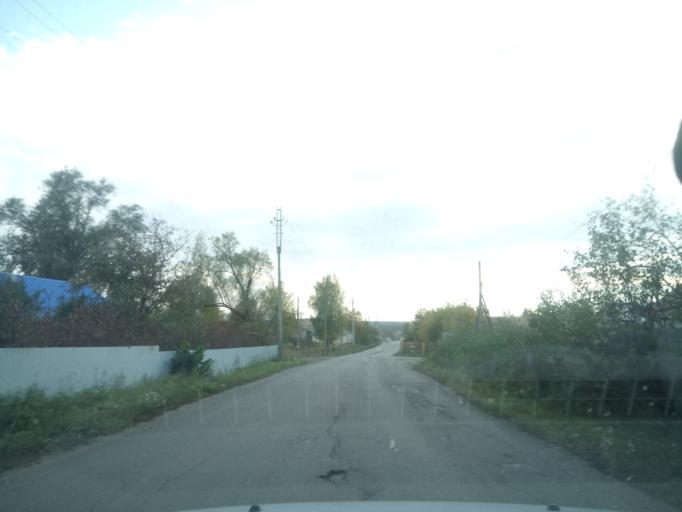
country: RU
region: Nizjnij Novgorod
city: Bol'shoye Boldino
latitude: 54.9964
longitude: 45.3146
